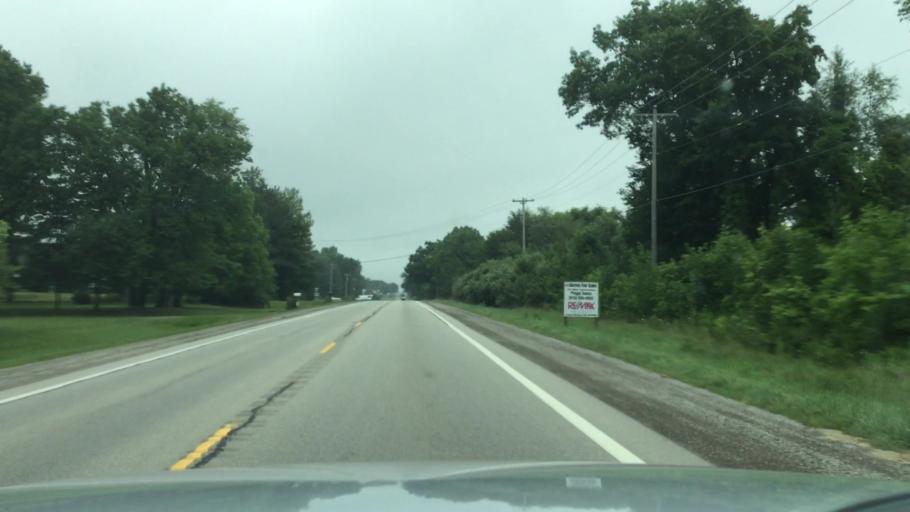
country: US
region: Michigan
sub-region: Shiawassee County
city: Durand
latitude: 42.9731
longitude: -83.9287
